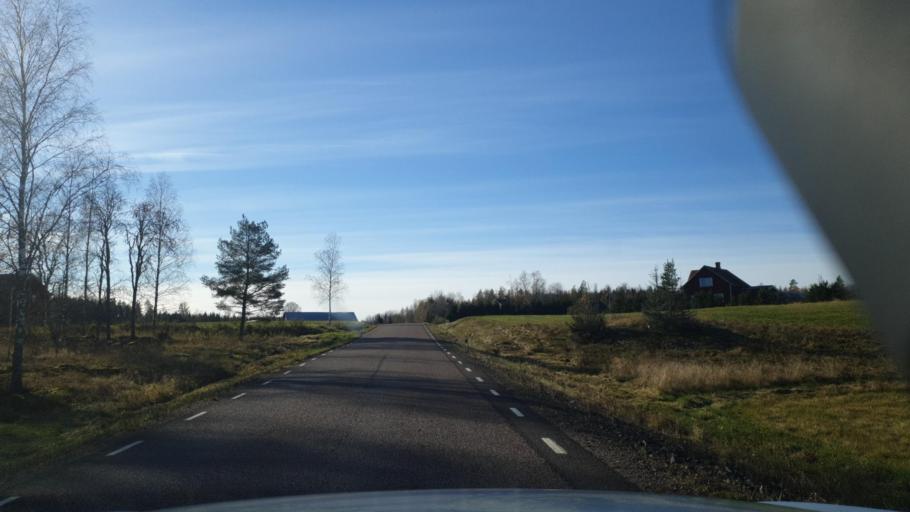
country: SE
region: Vaermland
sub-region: Karlstads Kommun
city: Edsvalla
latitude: 59.4897
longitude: 13.0957
